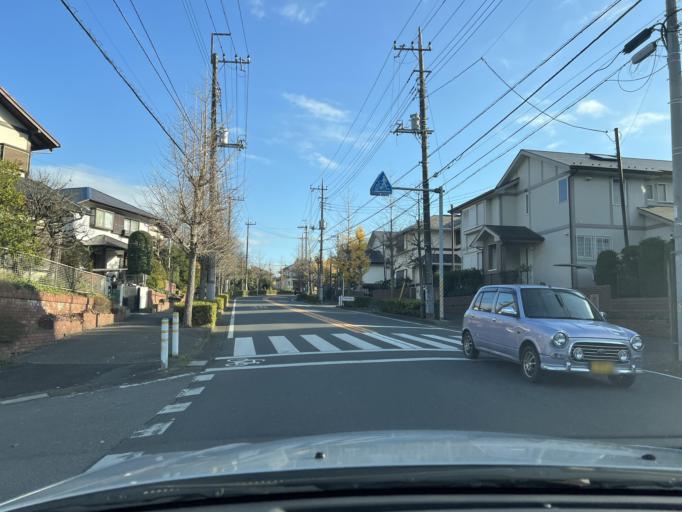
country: JP
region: Chiba
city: Kashiwa
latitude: 35.8984
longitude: 139.9665
